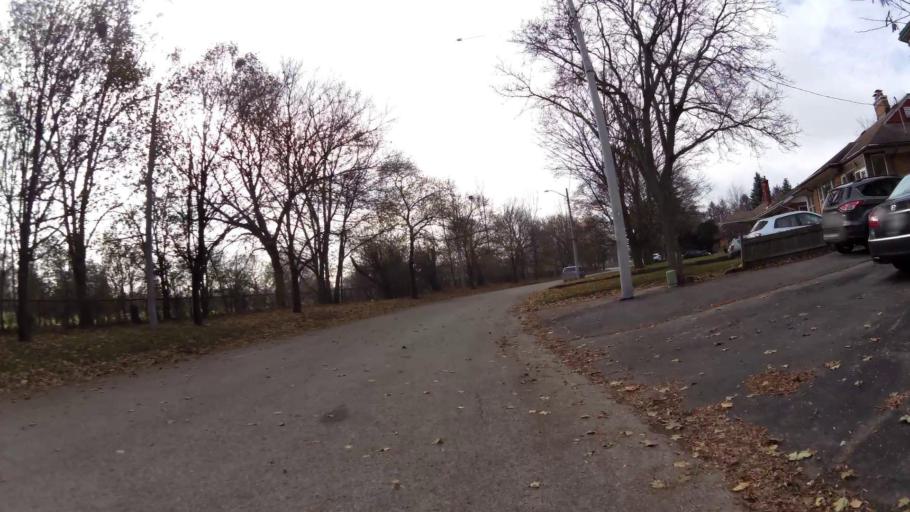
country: CA
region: Ontario
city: Kitchener
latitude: 43.4352
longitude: -80.4734
